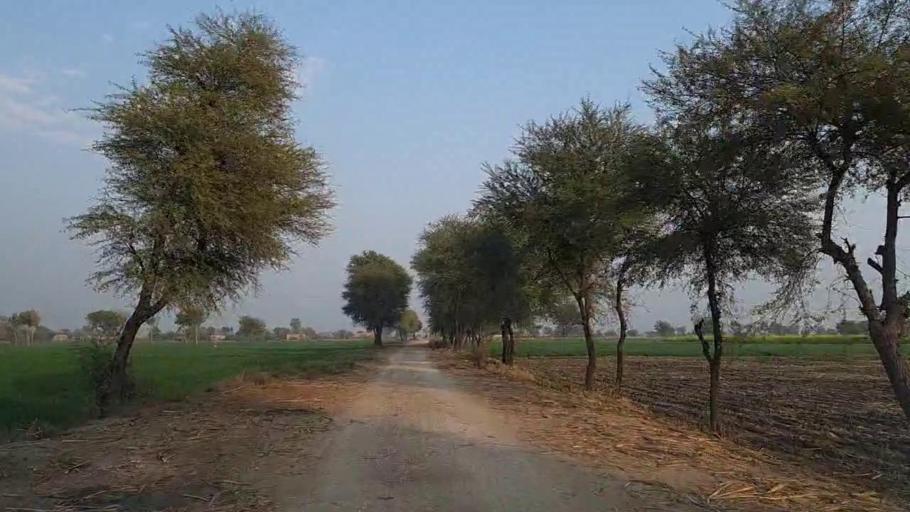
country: PK
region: Sindh
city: Jam Sahib
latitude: 26.3254
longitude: 68.5671
